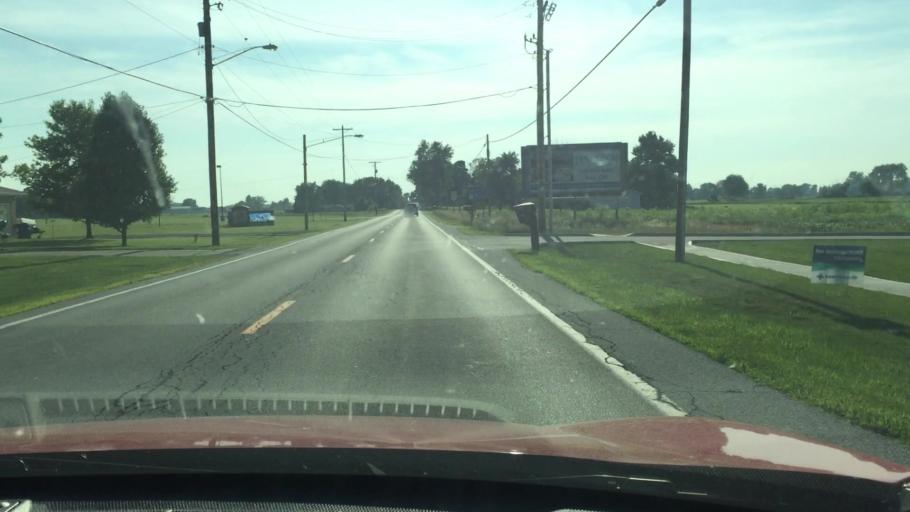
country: US
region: Ohio
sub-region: Hardin County
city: Ada
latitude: 40.7767
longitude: -83.8321
